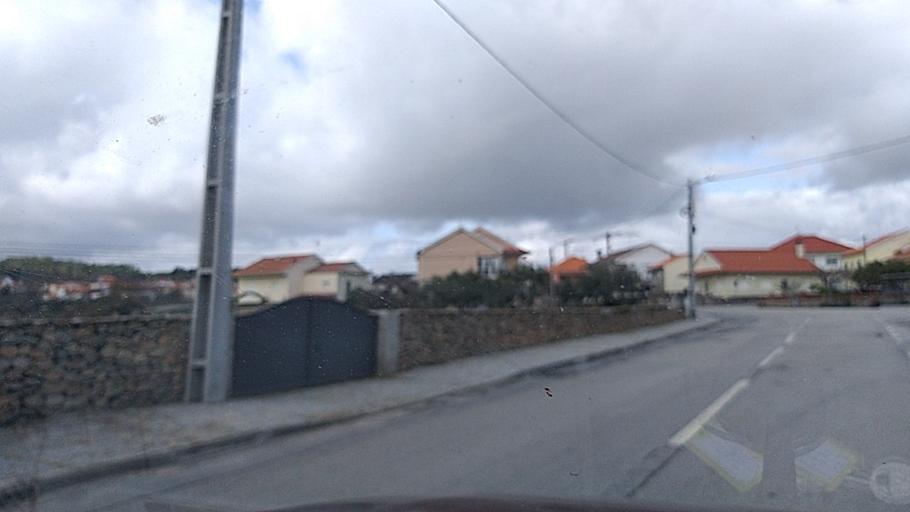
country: PT
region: Guarda
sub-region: Fornos de Algodres
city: Fornos de Algodres
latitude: 40.6613
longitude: -7.5620
